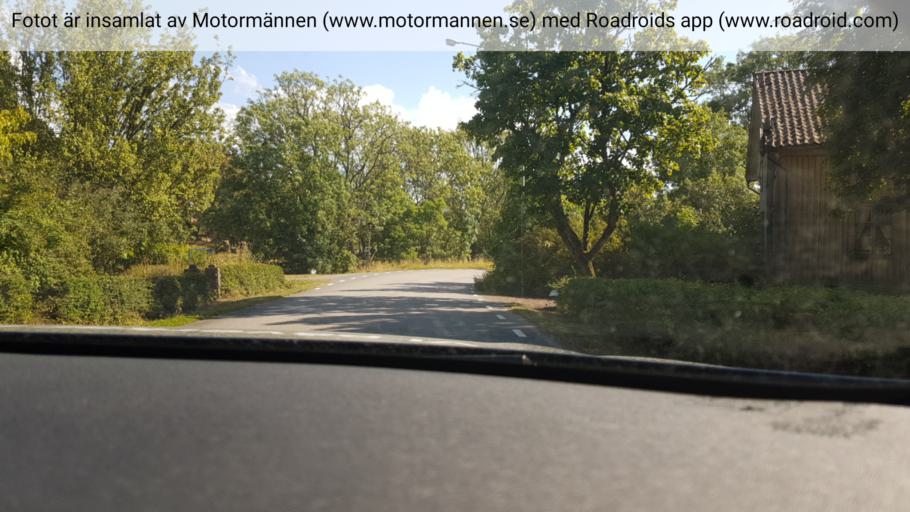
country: SE
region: Vaestra Goetaland
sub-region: Gotene Kommun
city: Kallby
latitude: 58.5597
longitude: 13.3501
